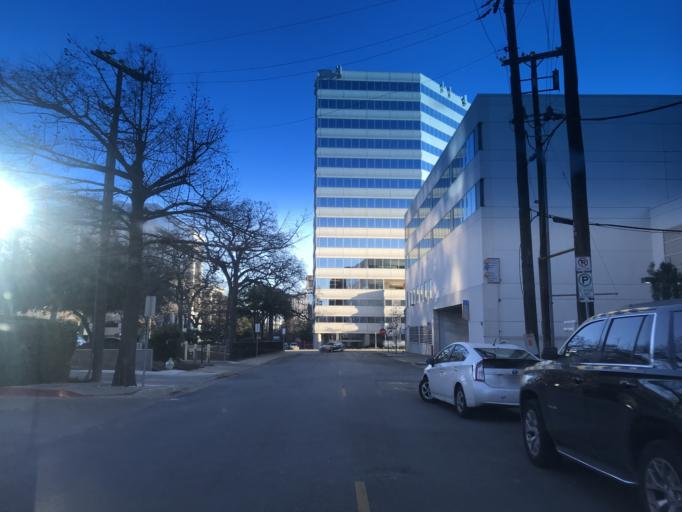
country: US
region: Texas
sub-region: Dallas County
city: Dallas
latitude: 32.8099
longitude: -96.8074
